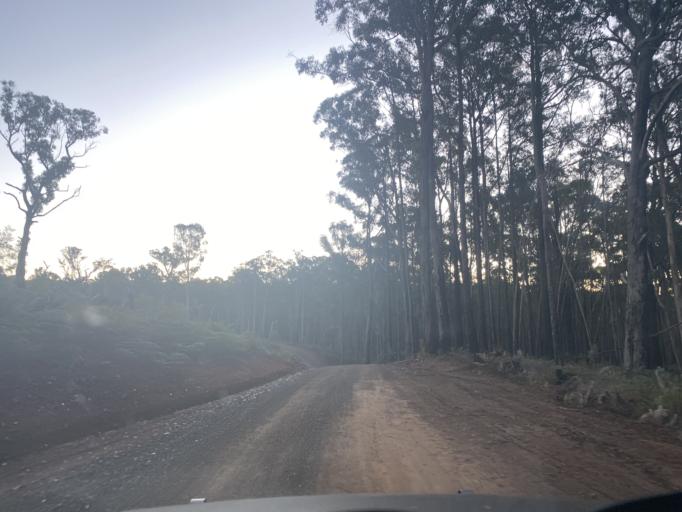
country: AU
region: Victoria
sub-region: Yarra Ranges
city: Healesville
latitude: -37.4240
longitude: 145.5246
